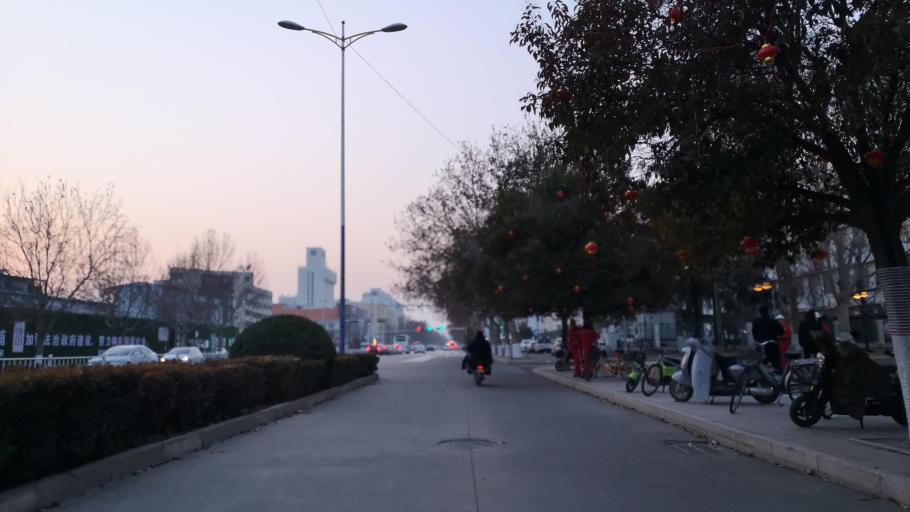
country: CN
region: Henan Sheng
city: Zhongyuanlu
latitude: 35.7765
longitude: 115.0725
